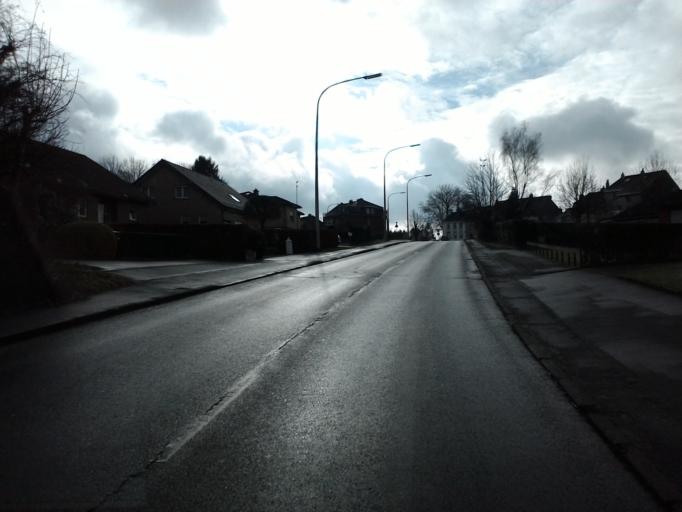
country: BE
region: Wallonia
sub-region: Province de Liege
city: Eupen
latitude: 50.6295
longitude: 6.0420
